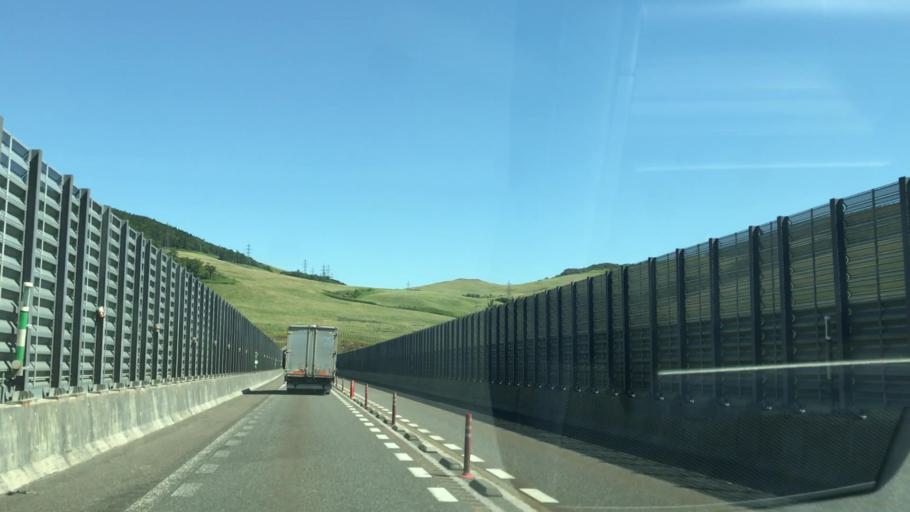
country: JP
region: Hokkaido
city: Shimo-furano
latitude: 43.0603
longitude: 142.7153
